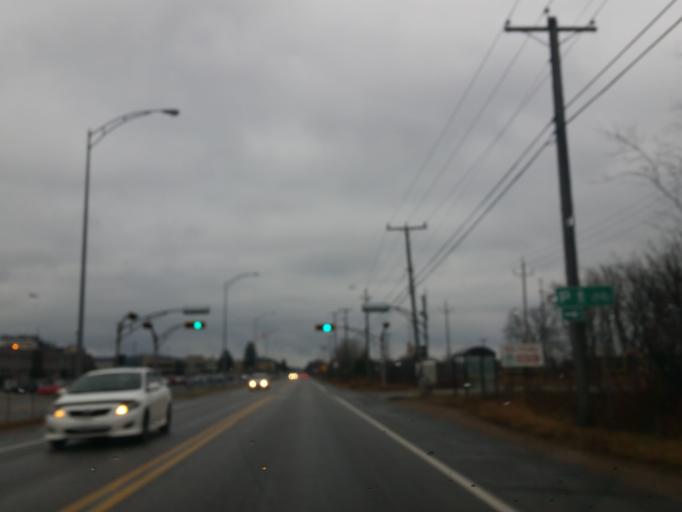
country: CA
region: Quebec
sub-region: Capitale-Nationale
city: Shannon
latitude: 46.8836
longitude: -71.4842
